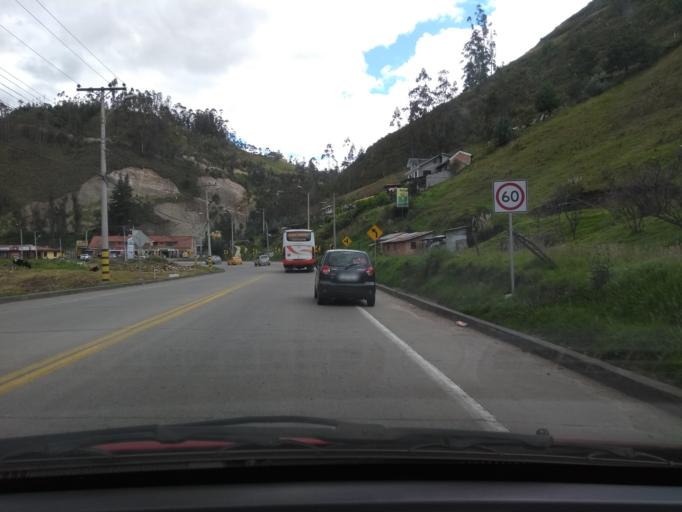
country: EC
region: Azuay
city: Cuenca
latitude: -2.9797
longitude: -79.0476
